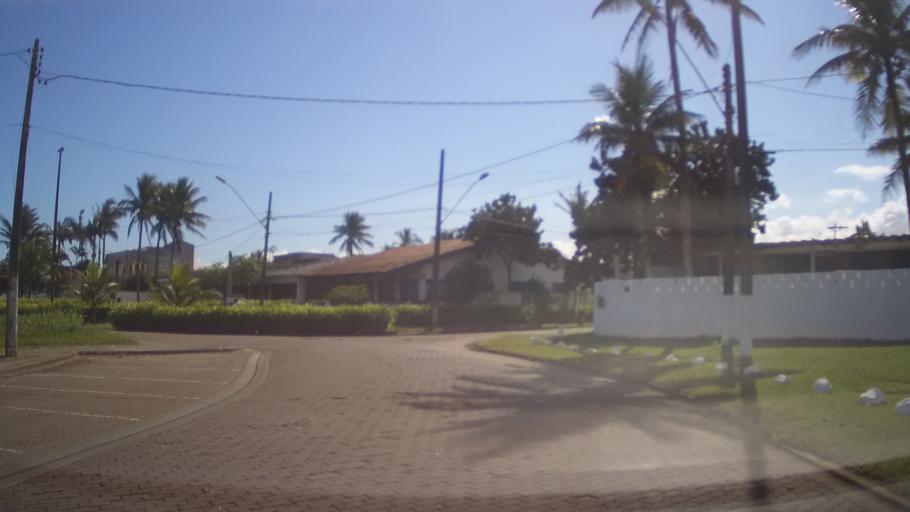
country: BR
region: Sao Paulo
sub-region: Itanhaem
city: Itanhaem
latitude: -24.2026
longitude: -46.8203
